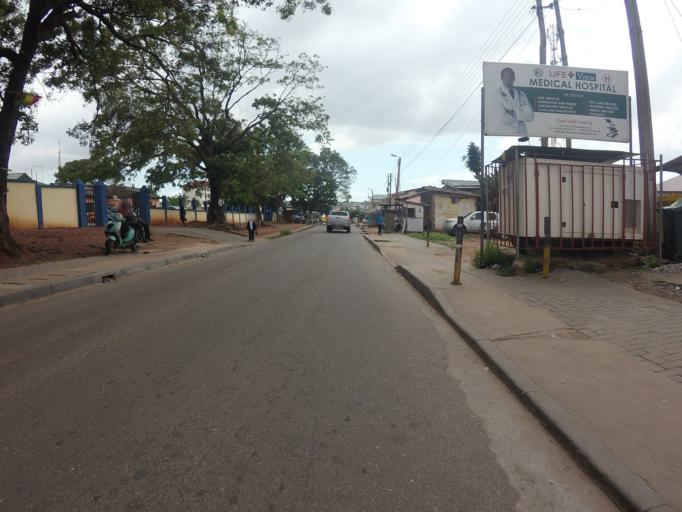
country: GH
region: Greater Accra
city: Accra
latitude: 5.5917
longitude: -0.2045
